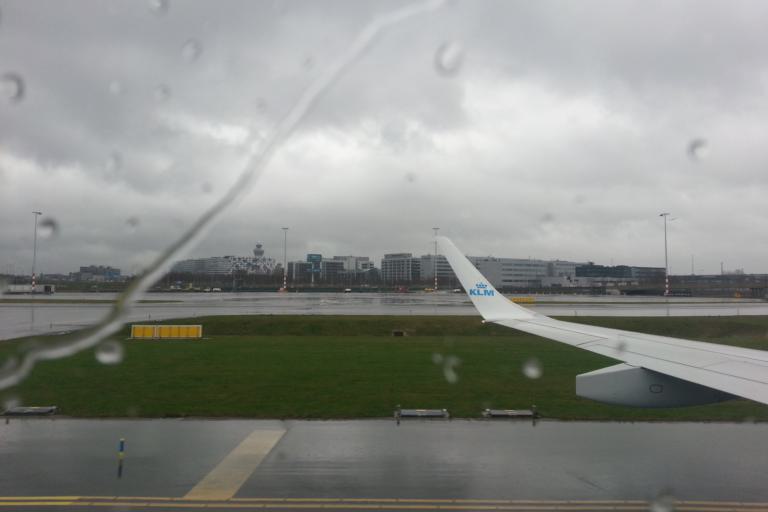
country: NL
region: North Holland
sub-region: Gemeente Aalsmeer
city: Aalsmeer
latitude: 52.3055
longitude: 4.7409
